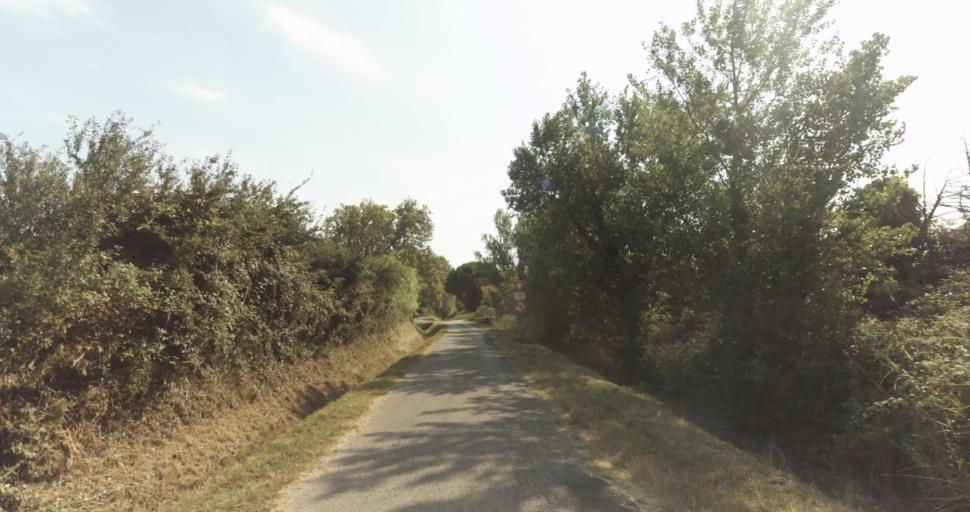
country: FR
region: Languedoc-Roussillon
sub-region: Departement des Pyrenees-Orientales
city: Latour-Bas-Elne
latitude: 42.6127
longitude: 3.0205
